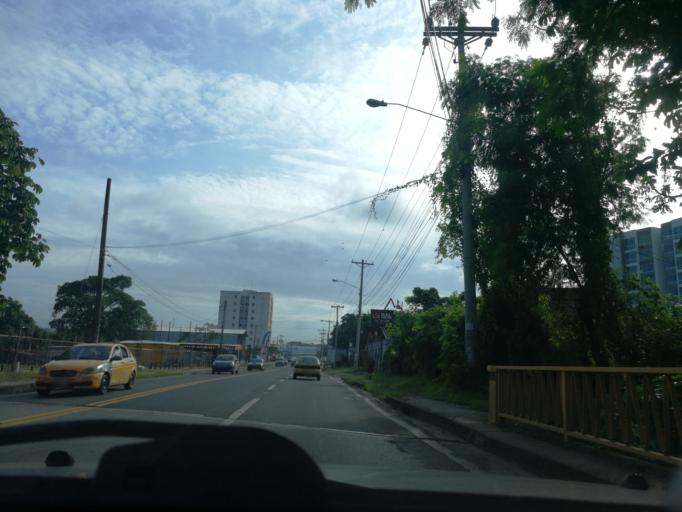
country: PA
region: Panama
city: Panama
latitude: 9.0201
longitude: -79.4998
